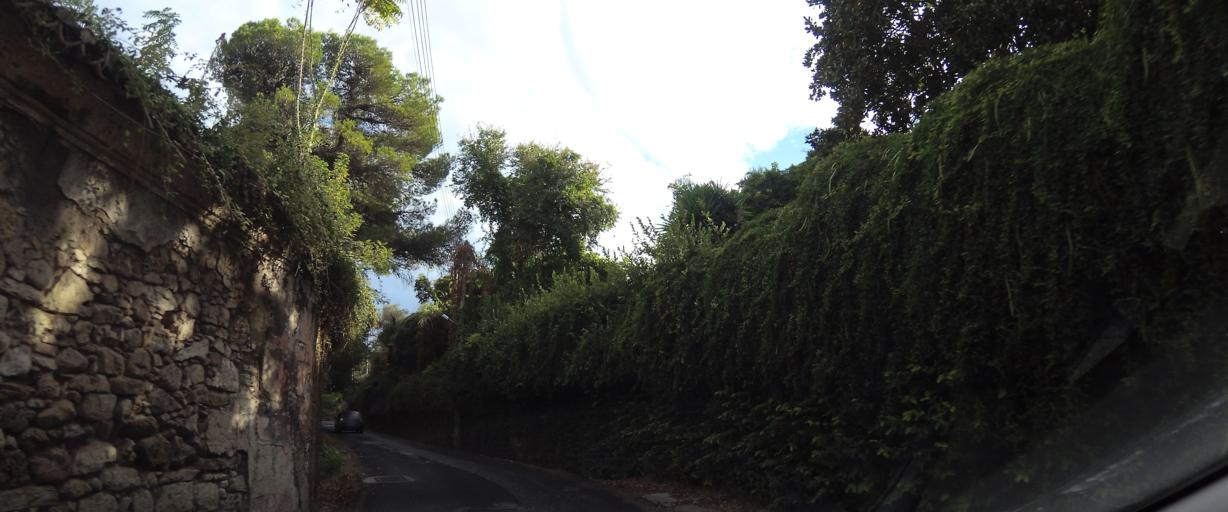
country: GR
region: Ionian Islands
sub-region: Nomos Kerkyras
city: Kerkyra
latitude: 39.6102
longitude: 19.9193
